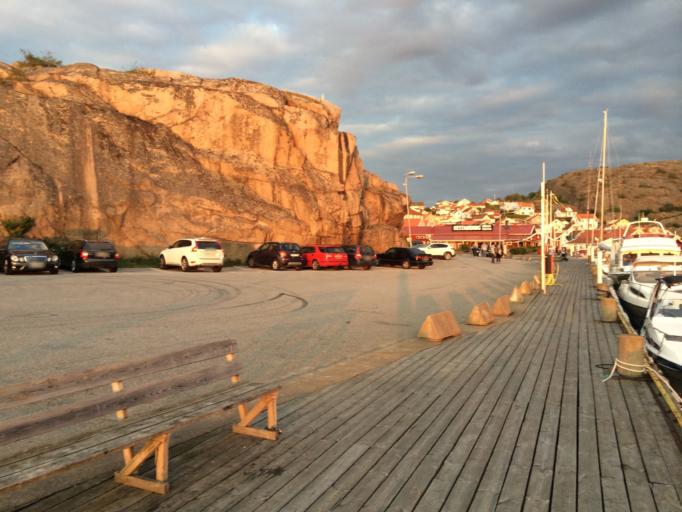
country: SE
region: Vaestra Goetaland
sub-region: Sotenas Kommun
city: Hunnebostrand
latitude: 58.4429
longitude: 11.2933
